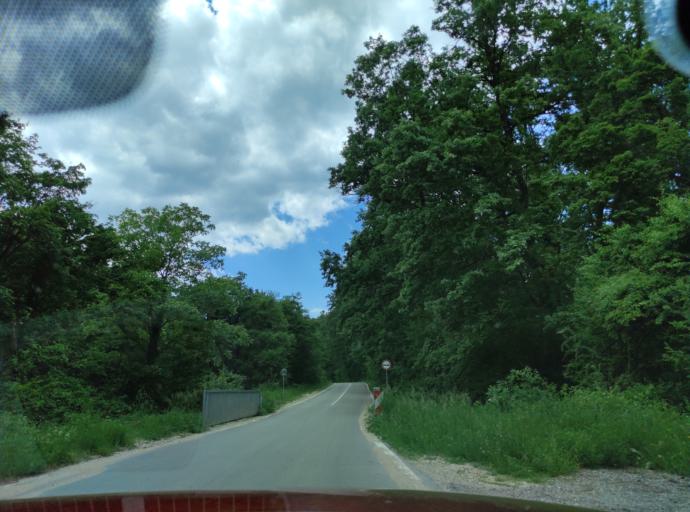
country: BG
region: Montana
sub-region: Obshtina Chiprovtsi
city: Chiprovtsi
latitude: 43.4627
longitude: 22.8884
